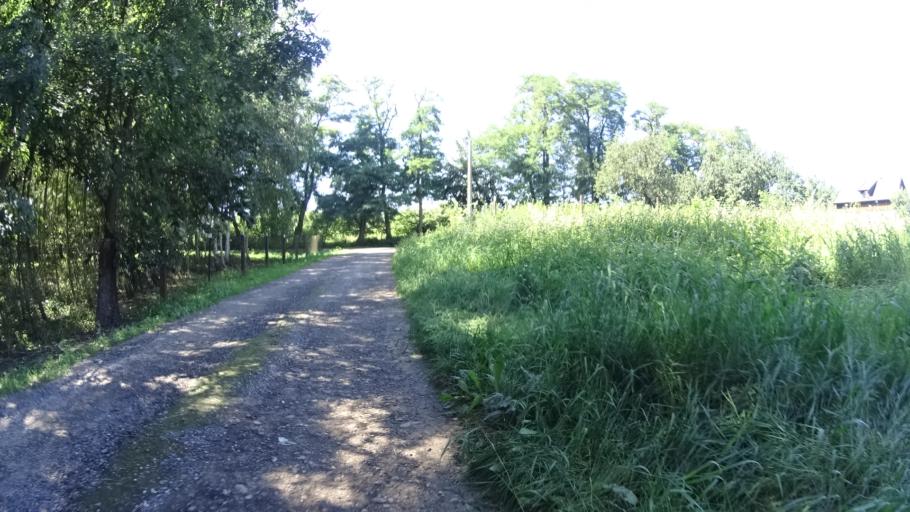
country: PL
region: Masovian Voivodeship
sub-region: Powiat bialobrzeski
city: Bialobrzegi
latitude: 51.6682
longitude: 20.8851
